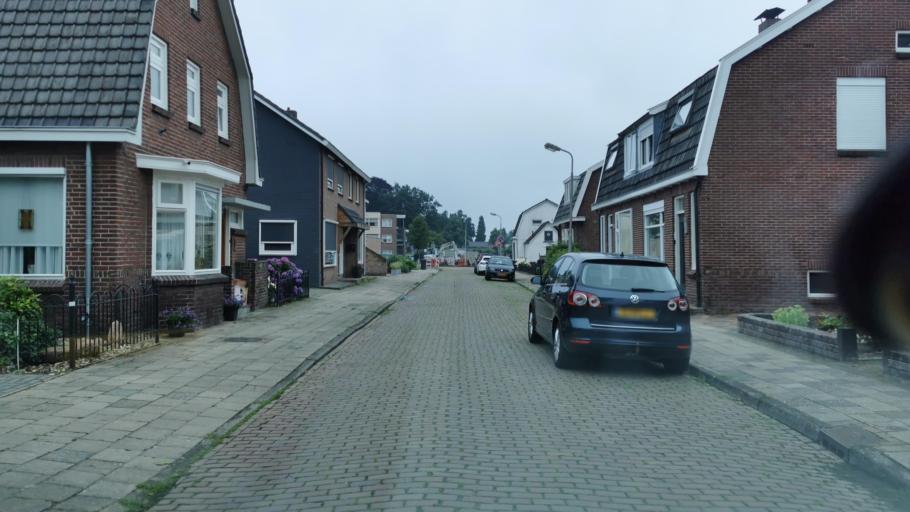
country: NL
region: Overijssel
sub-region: Gemeente Losser
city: Losser
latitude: 52.2600
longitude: 7.0102
